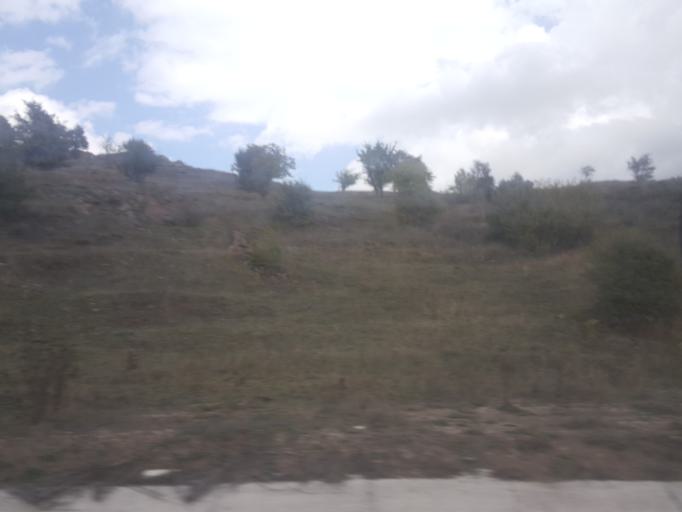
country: TR
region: Tokat
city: Bereketli
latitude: 40.5490
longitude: 37.2979
